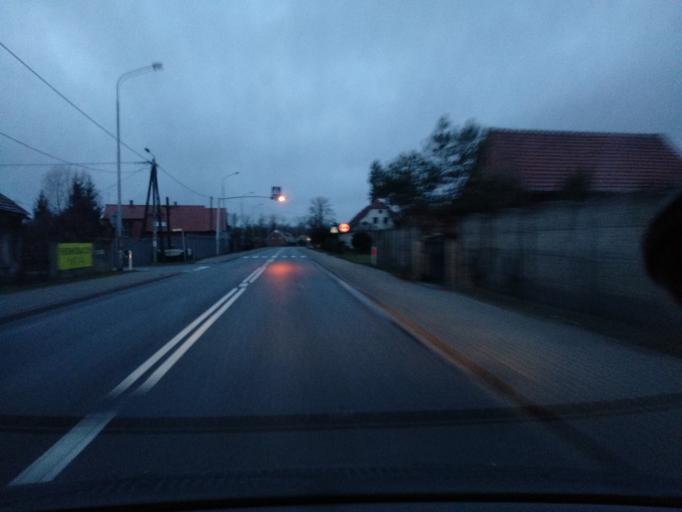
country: PL
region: Lower Silesian Voivodeship
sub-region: Powiat sredzki
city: Malczyce
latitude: 51.2018
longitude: 16.4786
